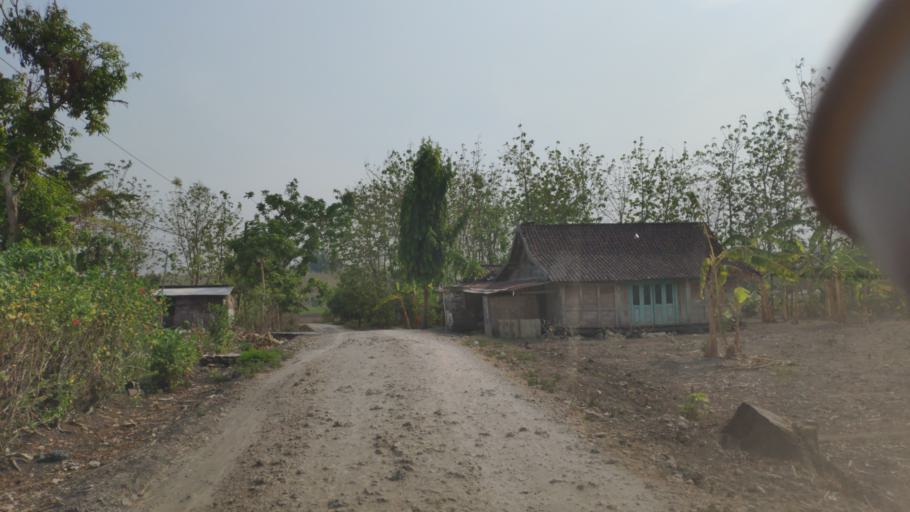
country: ID
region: Central Java
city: Randublatung
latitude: -7.2851
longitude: 111.2653
